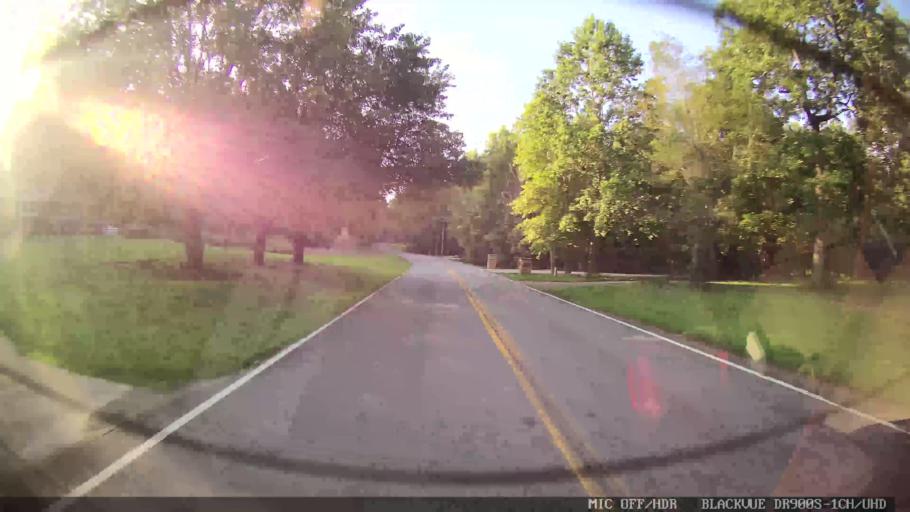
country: US
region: Georgia
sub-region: Bartow County
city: Emerson
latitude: 34.2116
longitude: -84.6937
